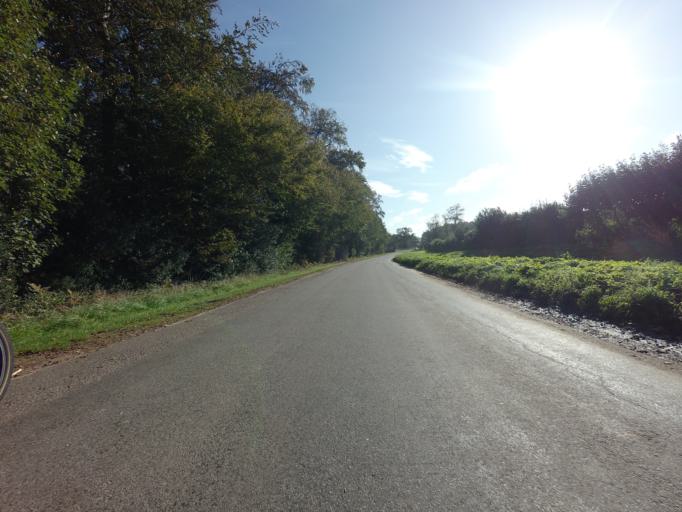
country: GB
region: England
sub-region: Norfolk
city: Dersingham
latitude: 52.8195
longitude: 0.6483
